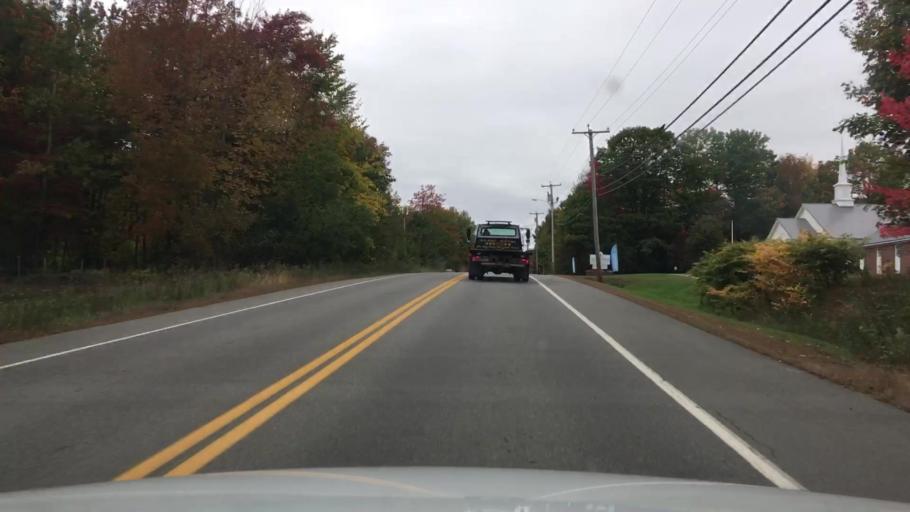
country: US
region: Maine
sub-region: Kennebec County
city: Oakland
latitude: 44.5547
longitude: -69.7355
